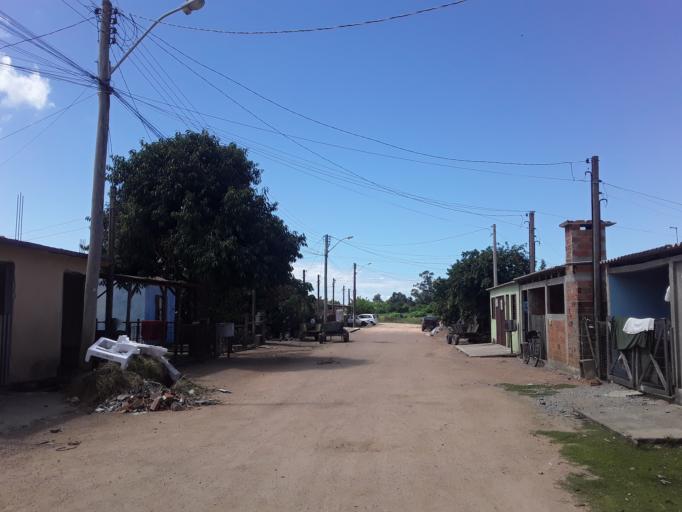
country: BR
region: Rio Grande do Sul
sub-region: Sao Lourenco Do Sul
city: Sao Lourenco do Sul
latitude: -31.3380
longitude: -51.9903
